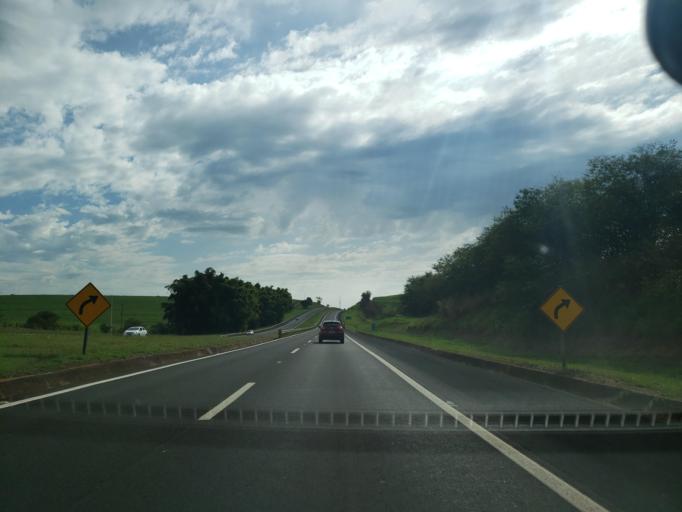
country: BR
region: Sao Paulo
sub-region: Cafelandia
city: Cafelandia
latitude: -21.8008
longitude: -49.6402
